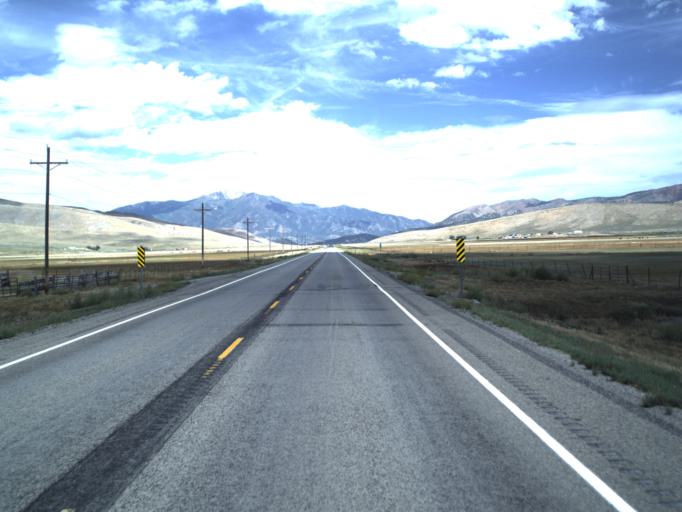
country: US
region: Utah
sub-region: Sanpete County
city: Fairview
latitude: 39.7828
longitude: -111.4930
